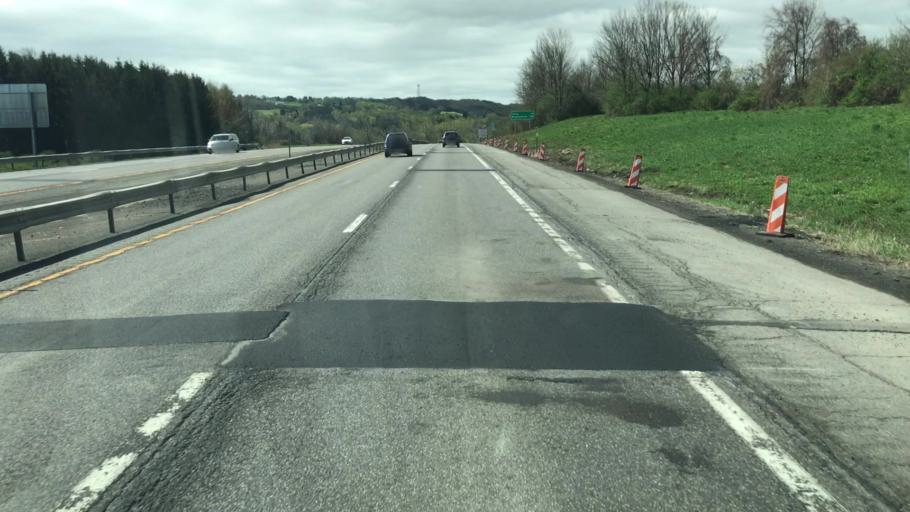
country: US
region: New York
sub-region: Onondaga County
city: Nedrow
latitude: 42.8769
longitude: -76.1104
